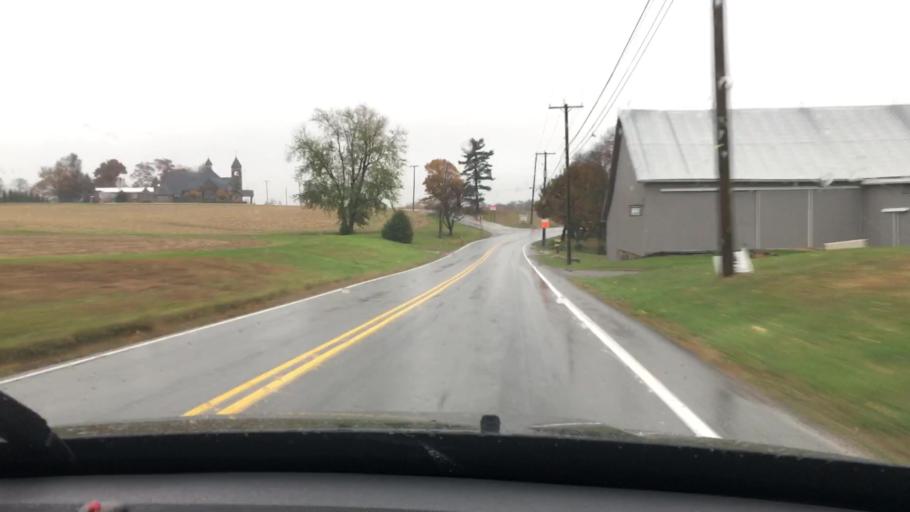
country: US
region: Pennsylvania
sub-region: York County
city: Stewartstown
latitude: 39.7264
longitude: -76.5202
